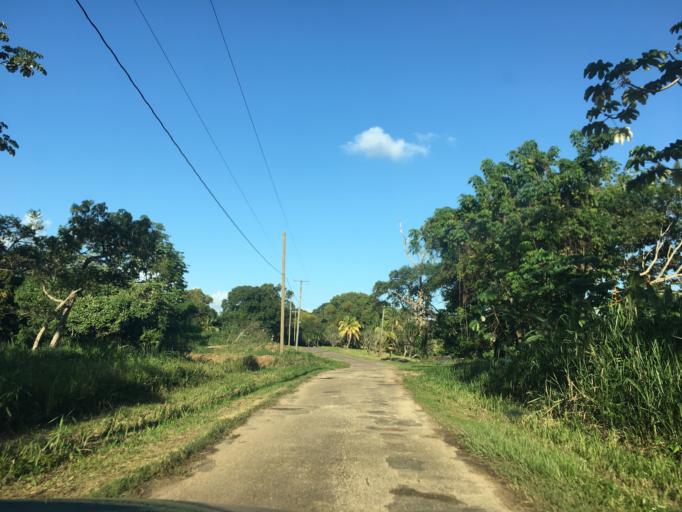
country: BZ
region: Stann Creek
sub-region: Dangriga
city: Dangriga
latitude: 16.8214
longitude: -88.3197
